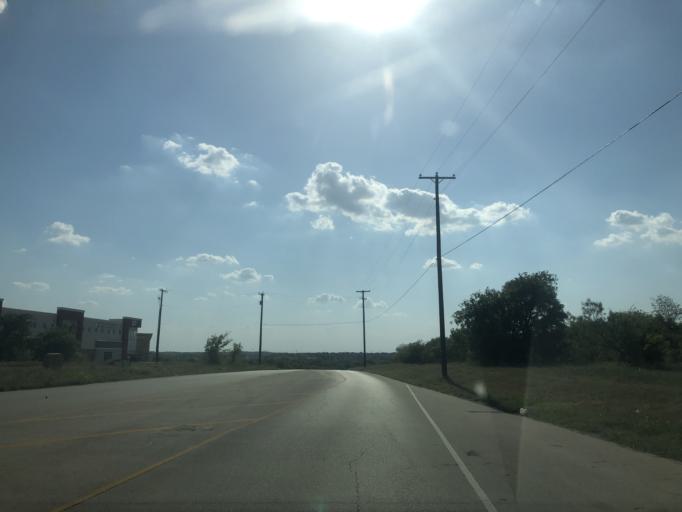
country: US
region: Texas
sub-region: Tarrant County
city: Saginaw
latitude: 32.8480
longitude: -97.3871
